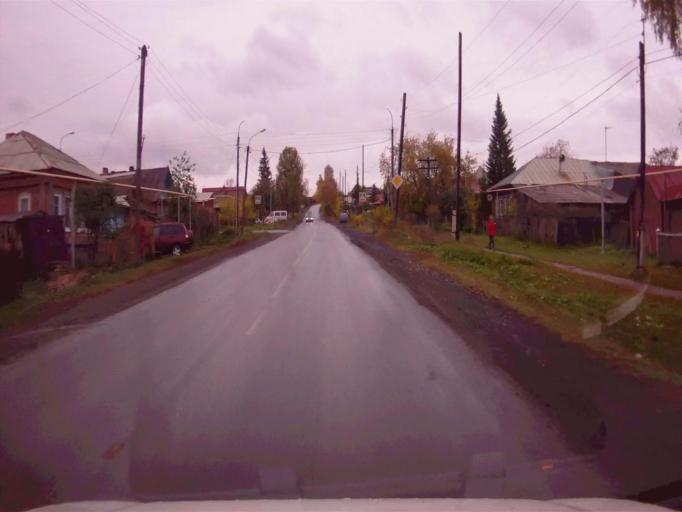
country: RU
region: Chelyabinsk
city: Verkhniy Ufaley
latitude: 56.0488
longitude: 60.2071
